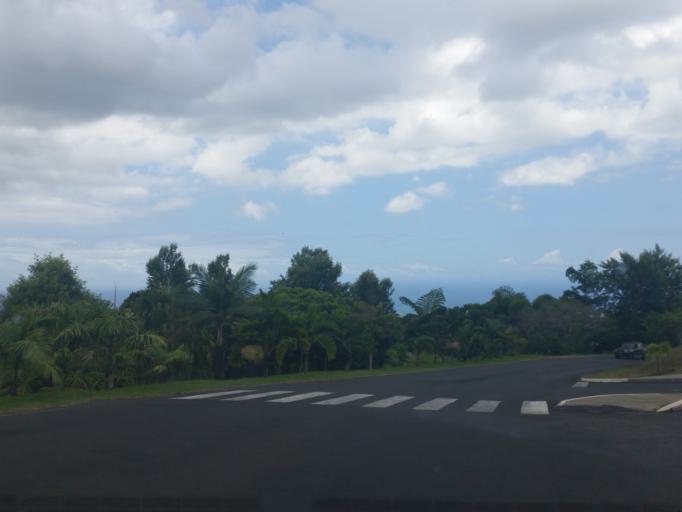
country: RE
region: Reunion
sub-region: Reunion
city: L'Entre-Deux
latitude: -21.2552
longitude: 55.4951
